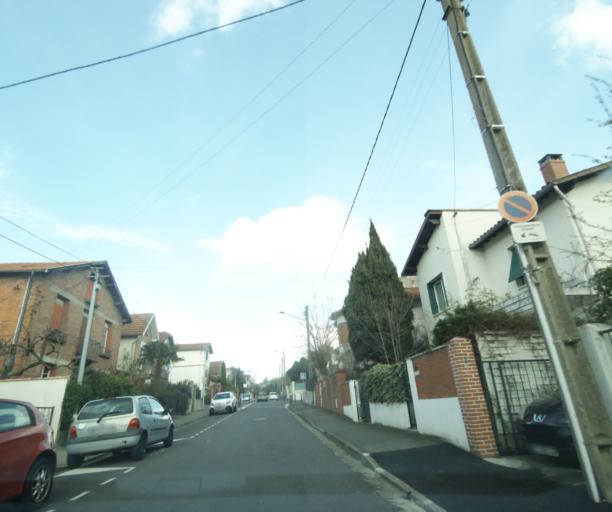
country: FR
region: Midi-Pyrenees
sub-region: Departement de la Haute-Garonne
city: Toulouse
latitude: 43.5852
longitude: 1.4715
